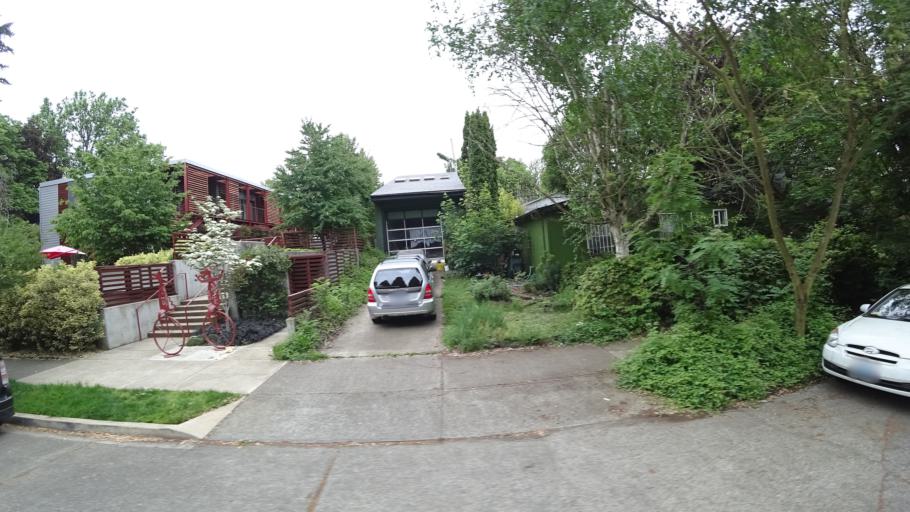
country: US
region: Oregon
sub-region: Multnomah County
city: Portland
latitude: 45.5178
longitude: -122.6392
